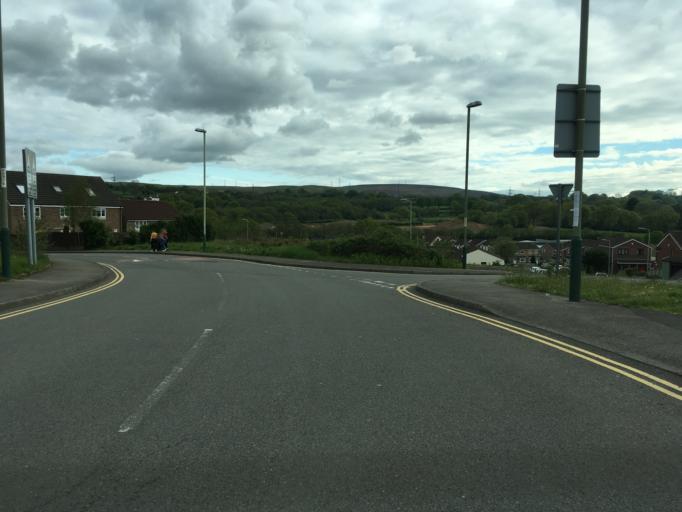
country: GB
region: Wales
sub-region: Caerphilly County Borough
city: Nelson
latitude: 51.6499
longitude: -3.2885
